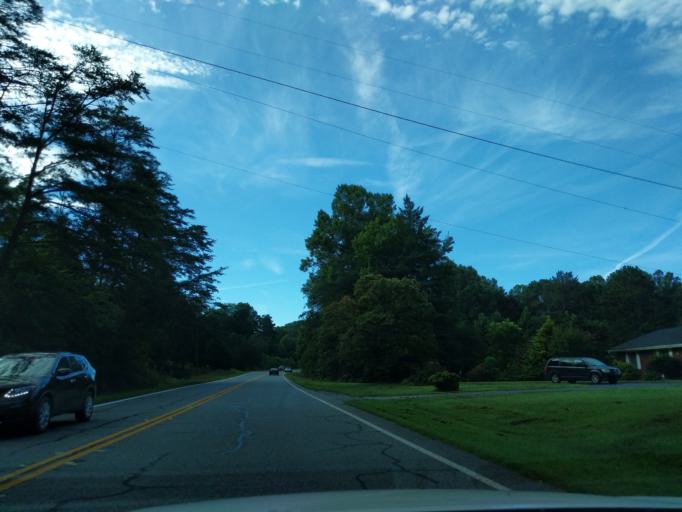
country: US
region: Georgia
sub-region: Fannin County
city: McCaysville
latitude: 34.9350
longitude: -84.3739
